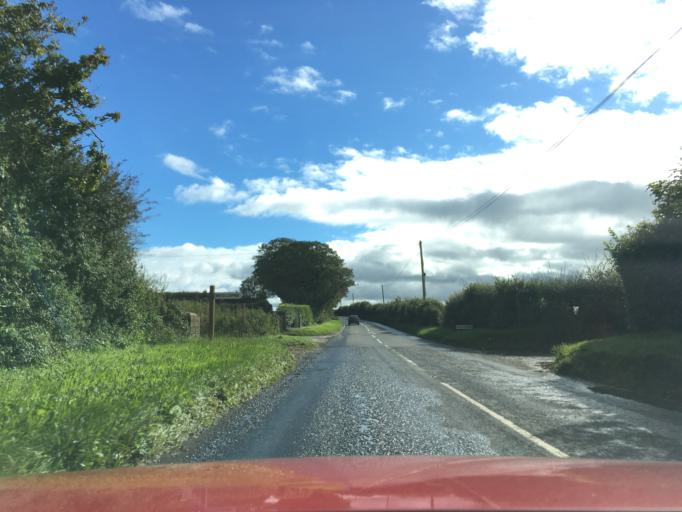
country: GB
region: England
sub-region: Devon
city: Kingsbridge
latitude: 50.3393
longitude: -3.7404
